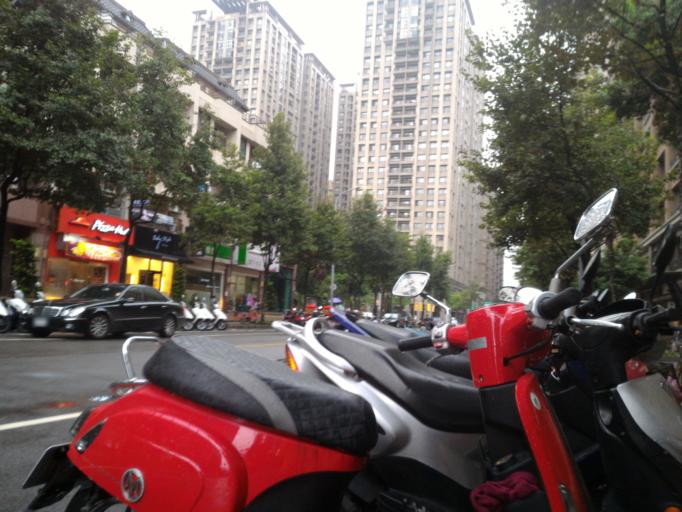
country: TW
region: Taiwan
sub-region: Taoyuan
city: Taoyuan
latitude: 24.9491
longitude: 121.3792
